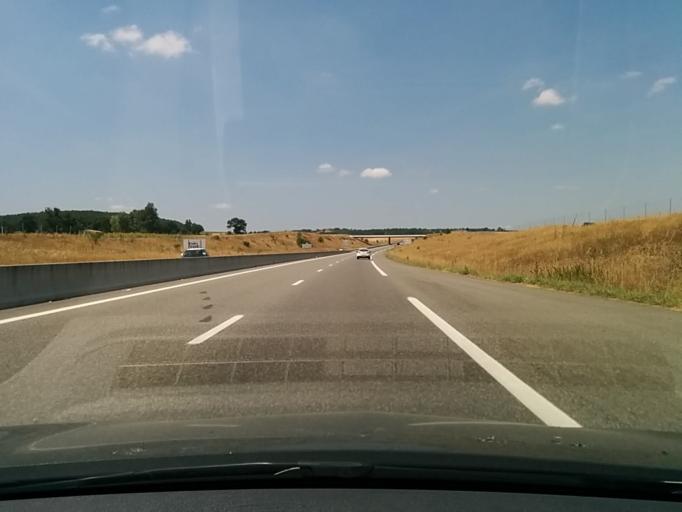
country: FR
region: Midi-Pyrenees
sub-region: Departement de la Haute-Garonne
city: Fontenilles
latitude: 43.5827
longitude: 1.1853
